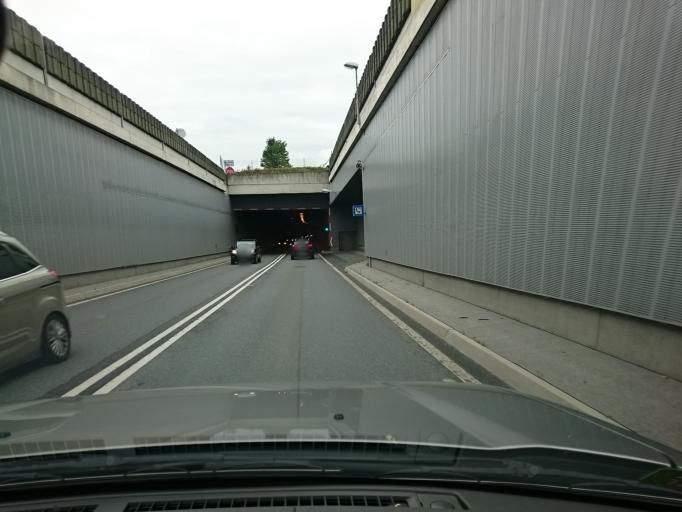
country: AT
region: Salzburg
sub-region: Politischer Bezirk Zell am See
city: Maishofen
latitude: 47.3665
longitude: 12.8032
